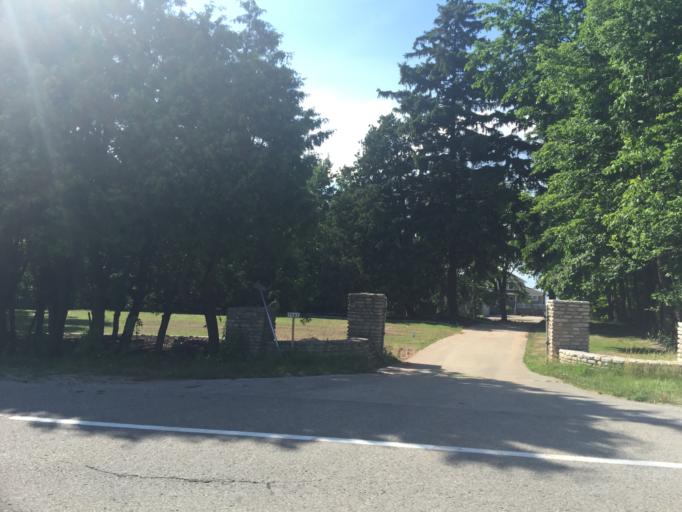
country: US
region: Wisconsin
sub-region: Door County
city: Sturgeon Bay
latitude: 45.0394
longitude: -87.3126
